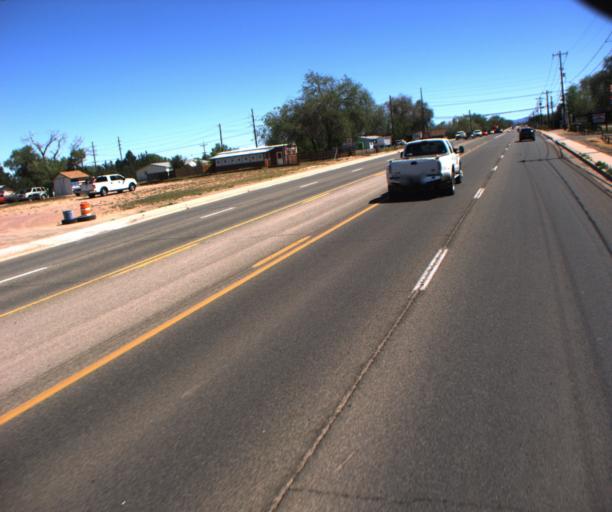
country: US
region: Arizona
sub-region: Yavapai County
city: Chino Valley
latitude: 34.7545
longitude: -112.4541
